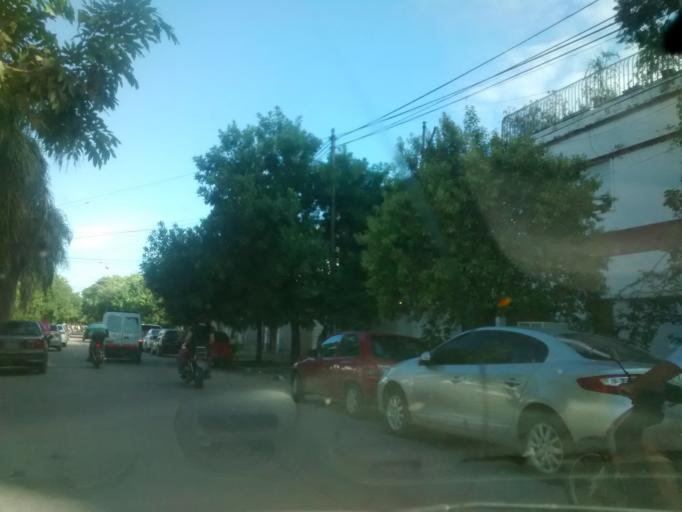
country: AR
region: Chaco
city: Resistencia
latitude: -27.4502
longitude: -58.9770
